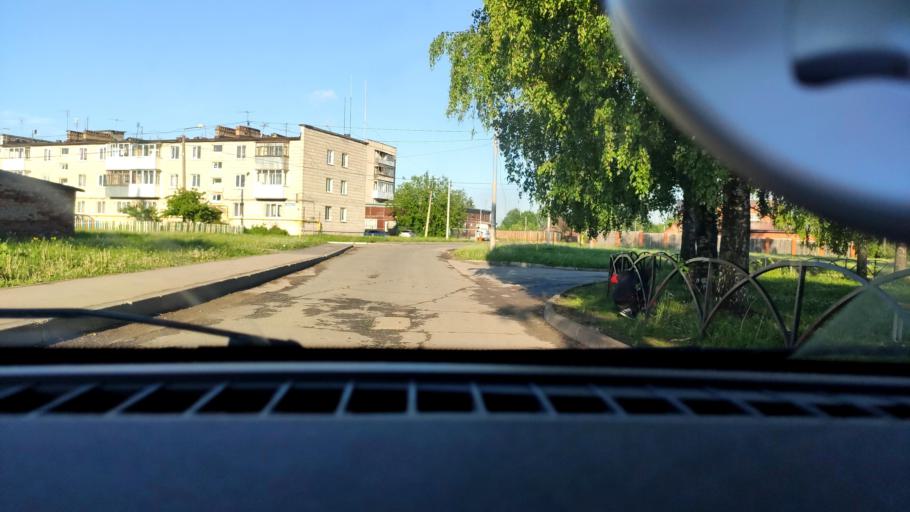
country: RU
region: Perm
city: Novyye Lyady
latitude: 58.0499
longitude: 56.5898
